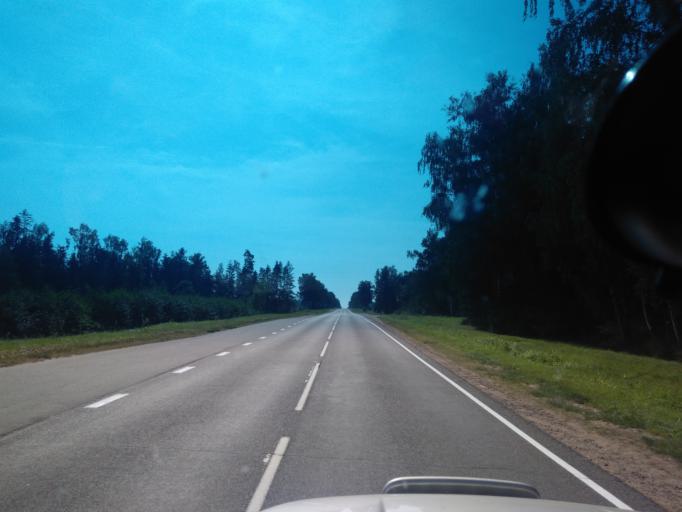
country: BY
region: Minsk
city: Uzda
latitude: 53.3539
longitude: 27.2256
